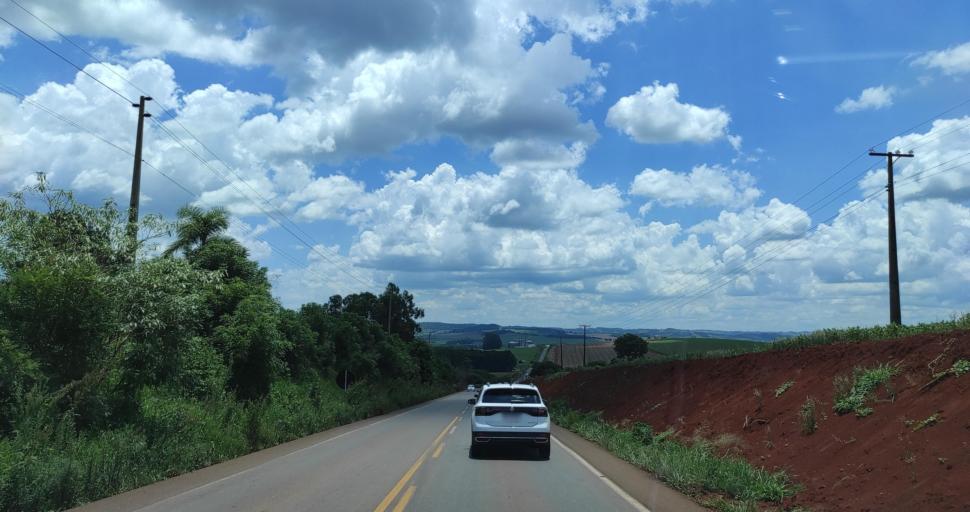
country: BR
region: Santa Catarina
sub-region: Xanxere
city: Xanxere
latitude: -26.7773
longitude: -52.4069
